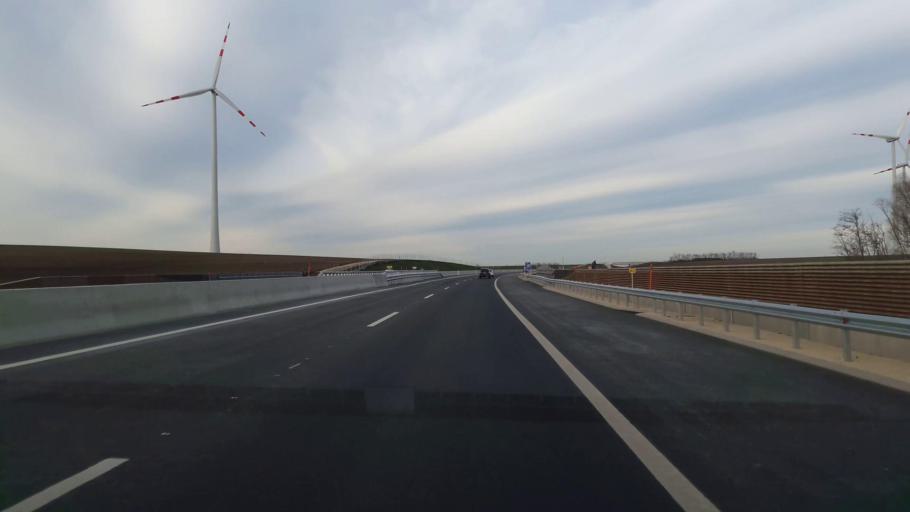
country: AT
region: Lower Austria
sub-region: Politischer Bezirk Mistelbach
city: Grosskrut
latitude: 48.6210
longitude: 16.6764
